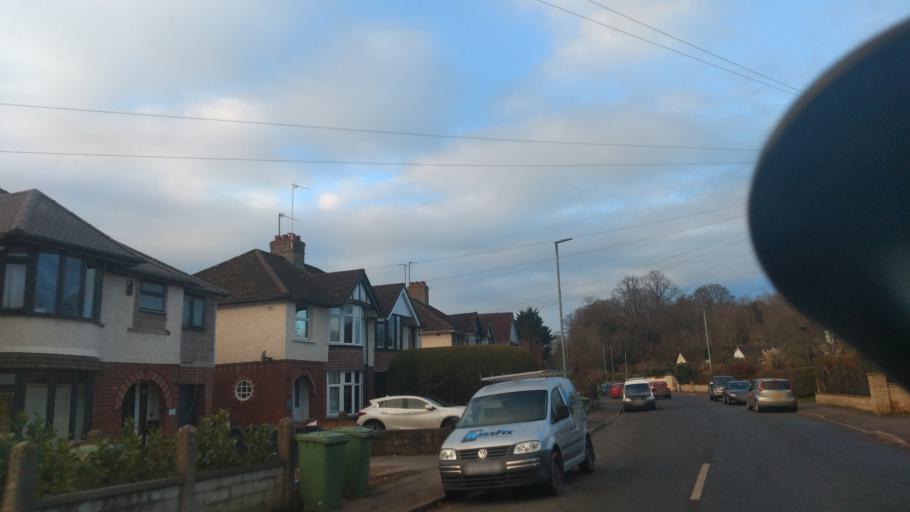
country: GB
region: England
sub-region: Somerset
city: Frome
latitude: 51.2350
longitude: -2.3139
